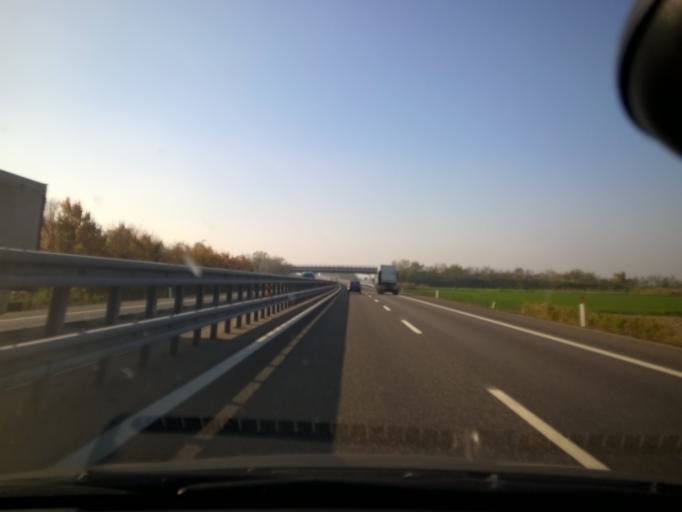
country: IT
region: Lombardy
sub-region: Provincia di Pavia
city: Pizzale
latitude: 45.0237
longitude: 9.0517
